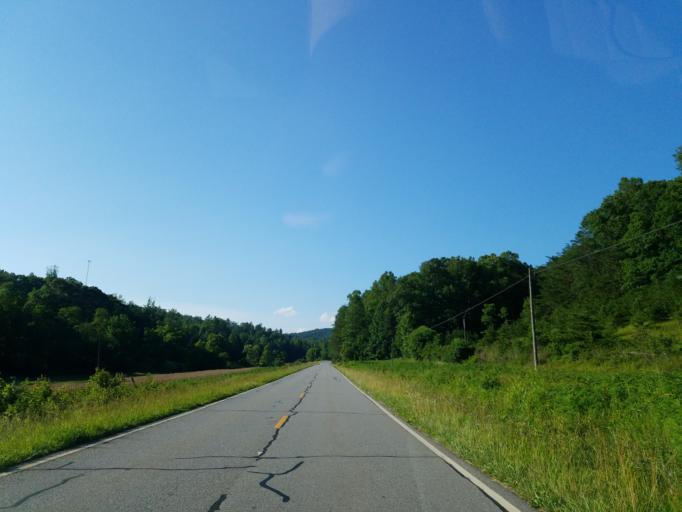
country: US
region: Georgia
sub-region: Fannin County
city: Blue Ridge
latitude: 34.7895
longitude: -84.1837
